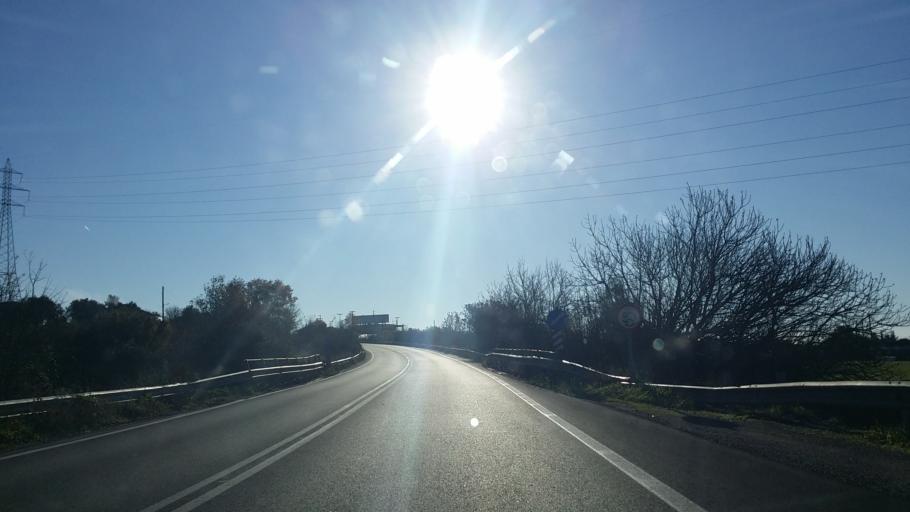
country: GR
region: West Greece
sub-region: Nomos Aitolias kai Akarnanias
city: Fitiai
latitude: 38.6914
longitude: 21.2257
